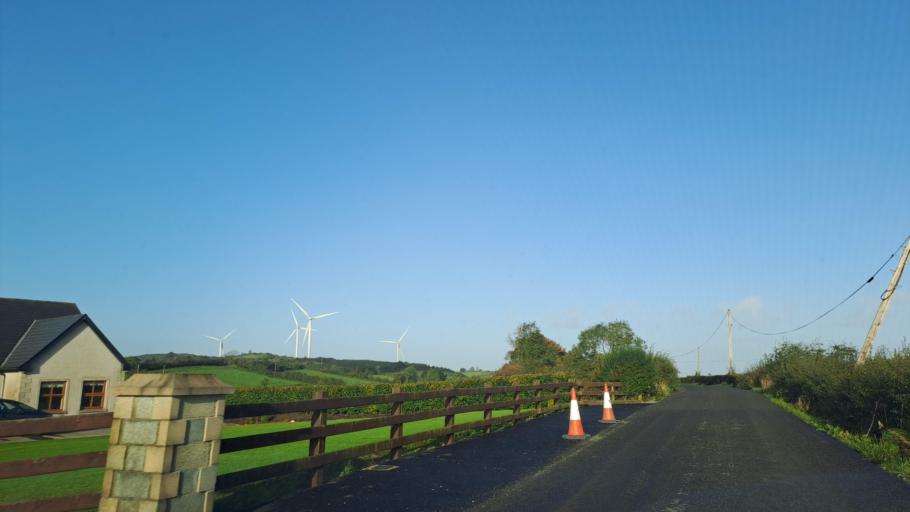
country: IE
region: Ulster
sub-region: County Monaghan
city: Castleblayney
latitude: 54.0808
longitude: -6.8488
